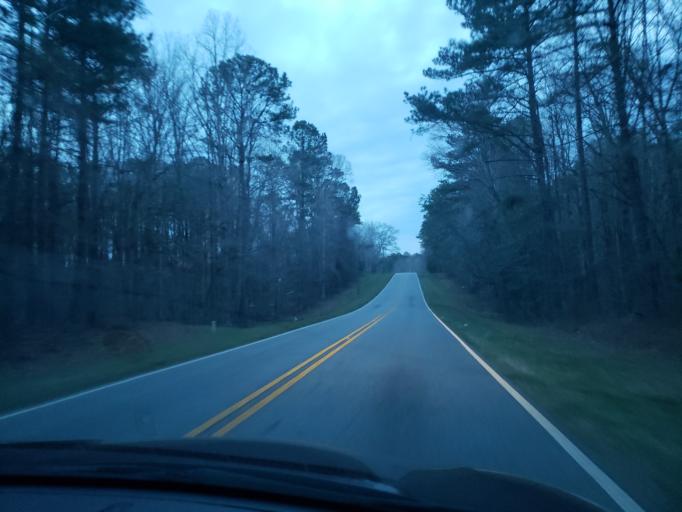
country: US
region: Alabama
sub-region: Lee County
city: Auburn
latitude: 32.6418
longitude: -85.4612
